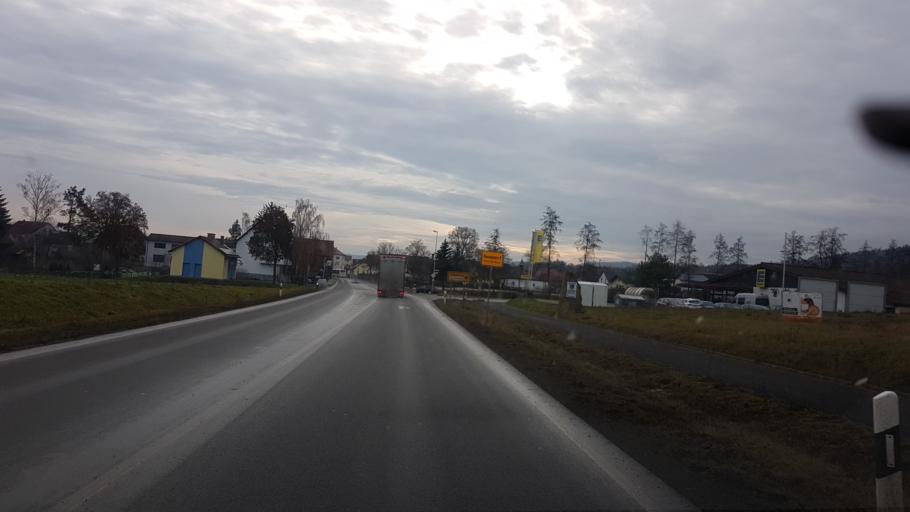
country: DE
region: Bavaria
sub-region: Upper Franconia
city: Reckendorf
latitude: 50.0238
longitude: 10.8264
